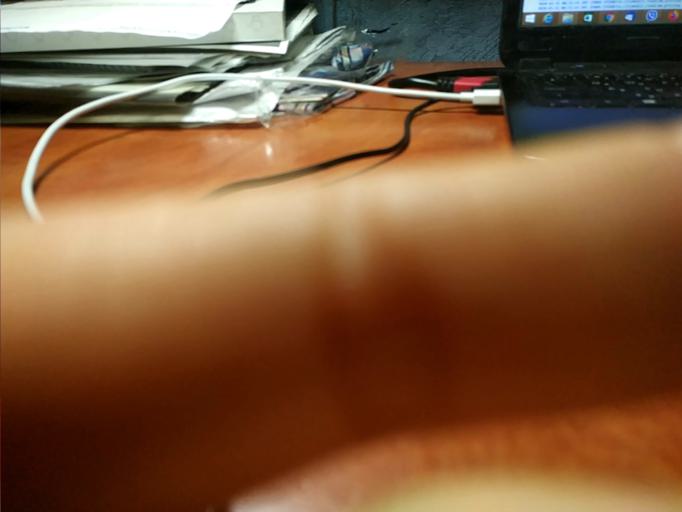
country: RU
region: Tverskaya
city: Rameshki
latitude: 57.3356
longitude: 35.9499
